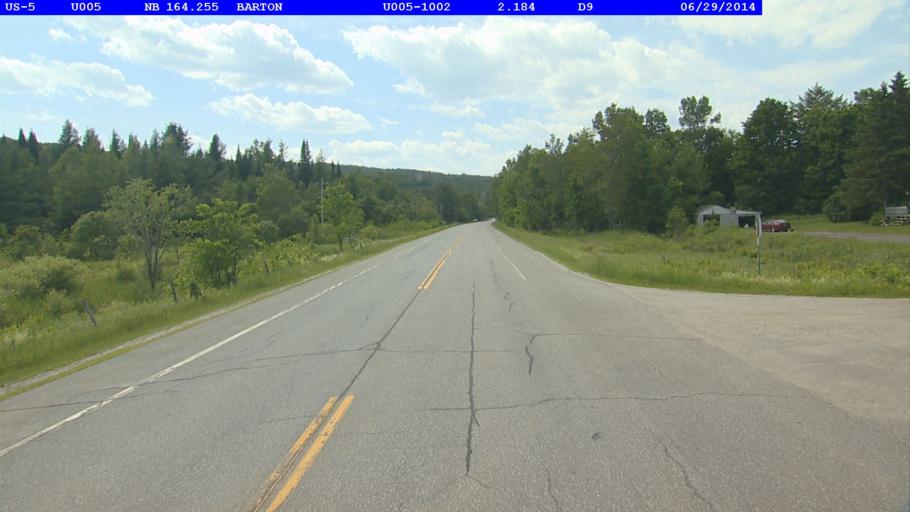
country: US
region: Vermont
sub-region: Caledonia County
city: Lyndonville
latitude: 44.7146
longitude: -72.1337
